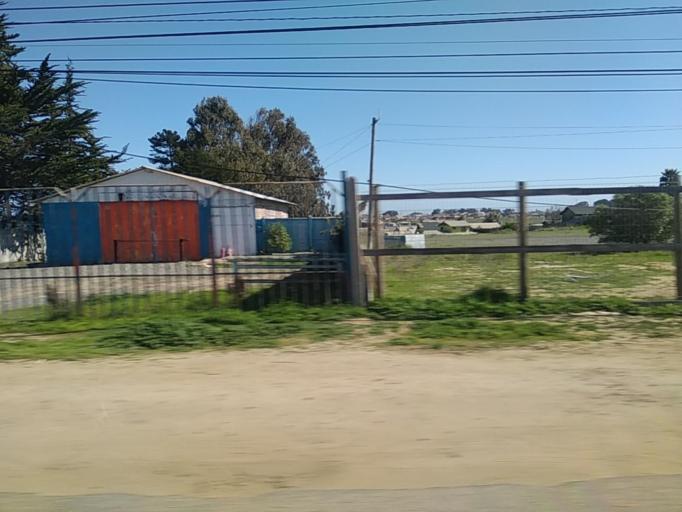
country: CL
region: Valparaiso
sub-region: San Antonio Province
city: El Tabo
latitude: -33.4324
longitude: -71.6875
